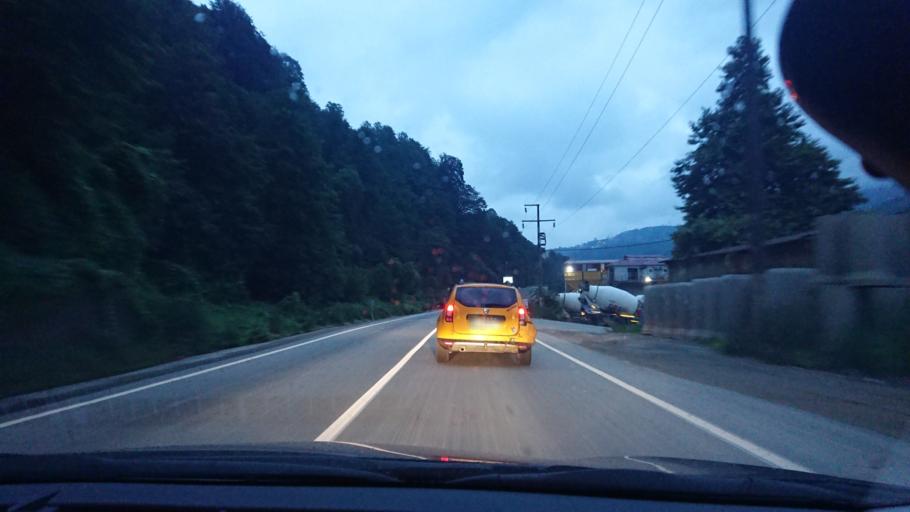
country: TR
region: Rize
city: Gundogdu
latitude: 41.0157
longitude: 40.5680
